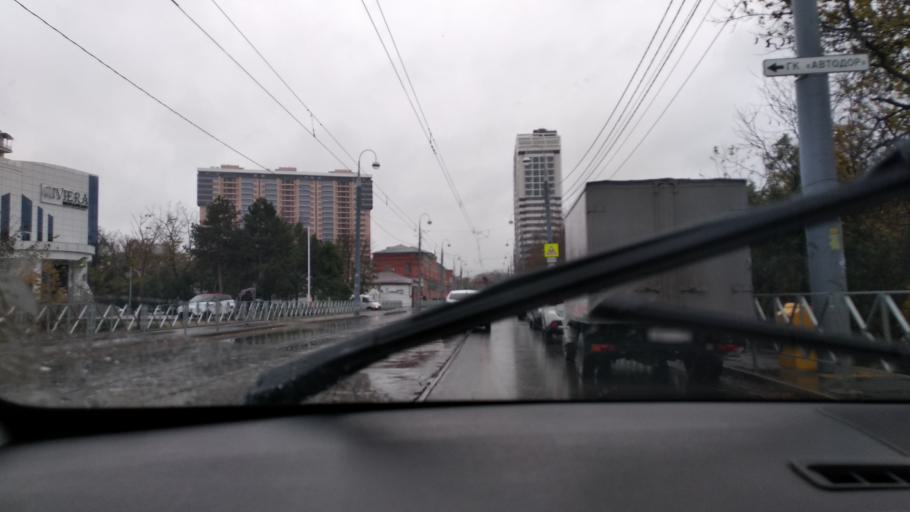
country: RU
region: Krasnodarskiy
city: Krasnodar
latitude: 45.0267
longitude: 38.9906
